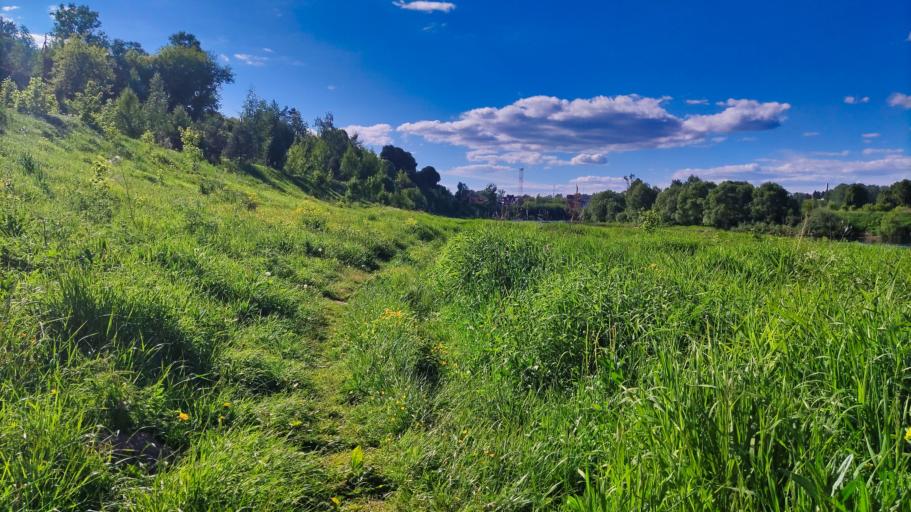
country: RU
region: Tverskaya
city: Rzhev
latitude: 56.2516
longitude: 34.3460
